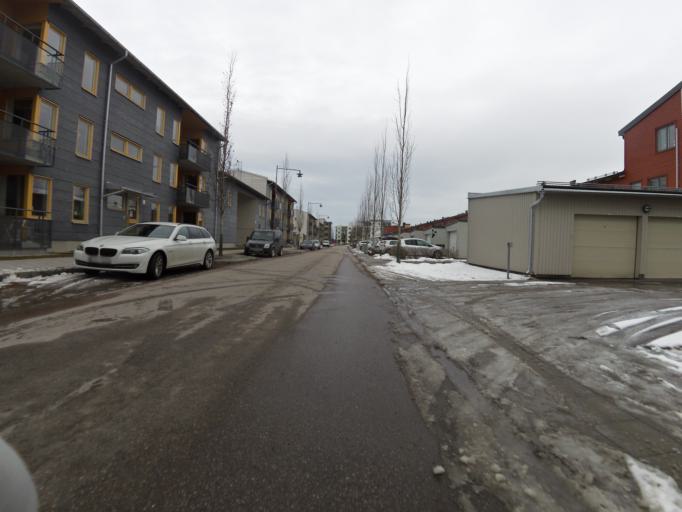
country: SE
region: Gaevleborg
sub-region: Gavle Kommun
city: Gavle
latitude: 60.6801
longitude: 17.1630
